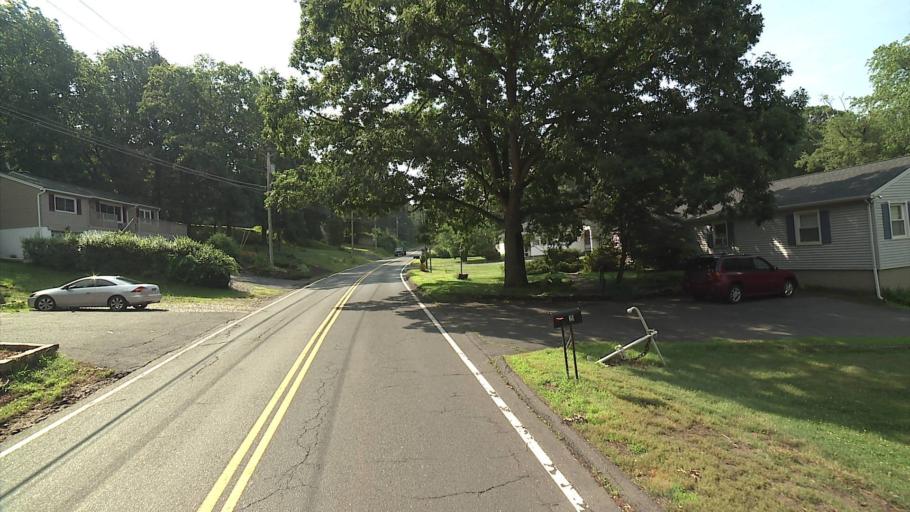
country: US
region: Connecticut
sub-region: New Haven County
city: Wolcott
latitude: 41.5953
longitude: -72.9594
